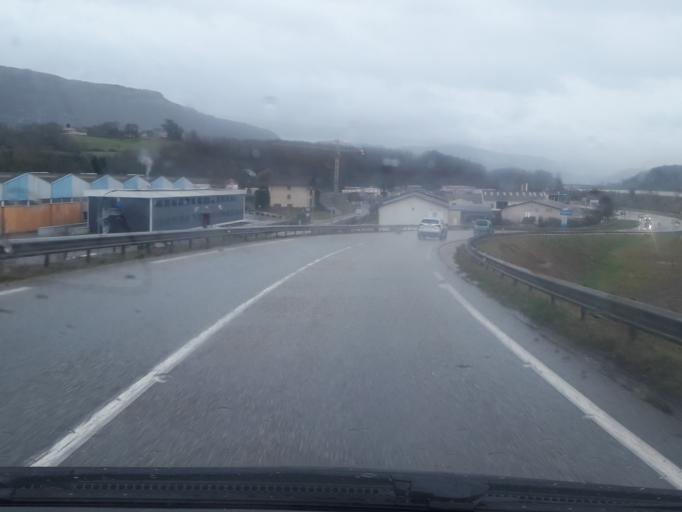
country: FR
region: Rhone-Alpes
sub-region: Departement de l'Ain
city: Belley
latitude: 45.7534
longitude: 5.7082
